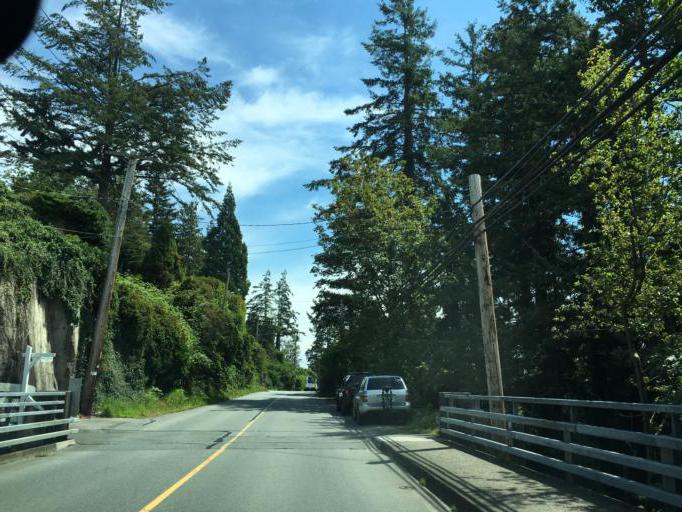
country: CA
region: British Columbia
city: West Vancouver
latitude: 49.3412
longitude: -123.2263
